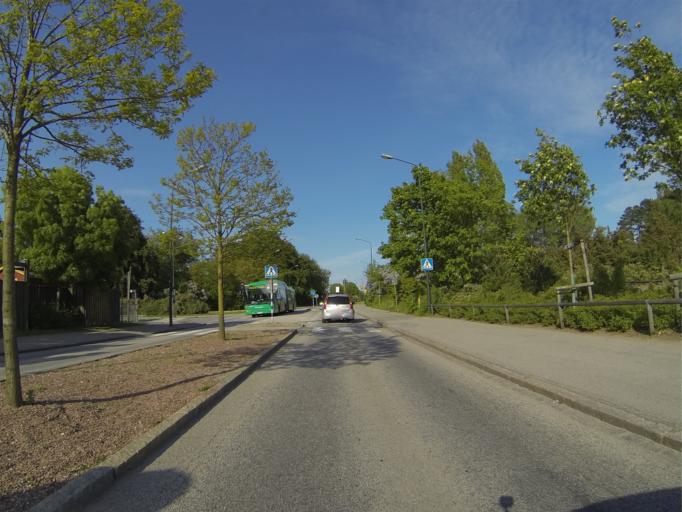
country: SE
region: Skane
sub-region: Burlovs Kommun
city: Arloev
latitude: 55.6081
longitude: 13.0496
